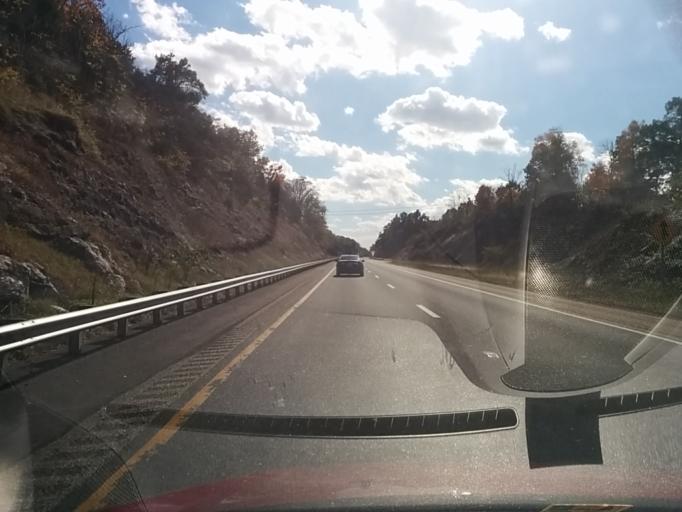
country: US
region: Virginia
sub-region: Rockbridge County
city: East Lexington
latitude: 37.8402
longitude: -79.3679
